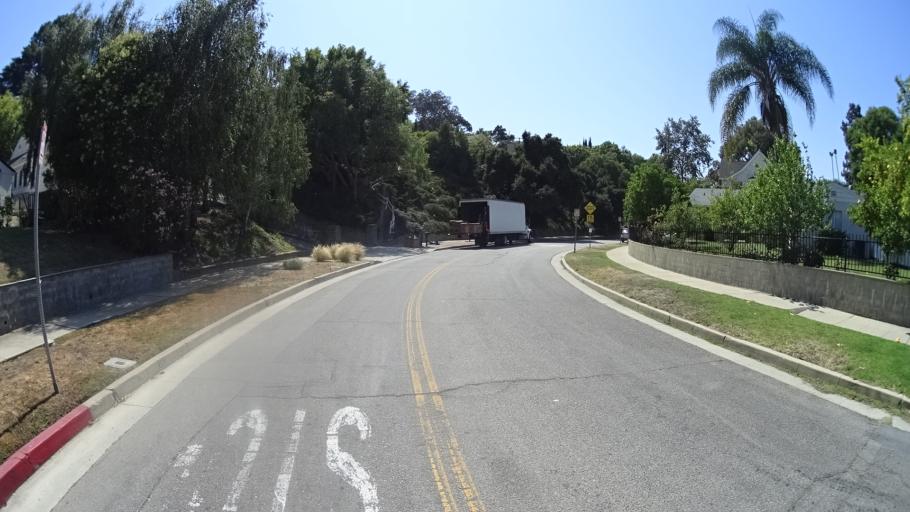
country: US
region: California
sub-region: Los Angeles County
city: North Hollywood
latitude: 34.1369
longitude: -118.3941
